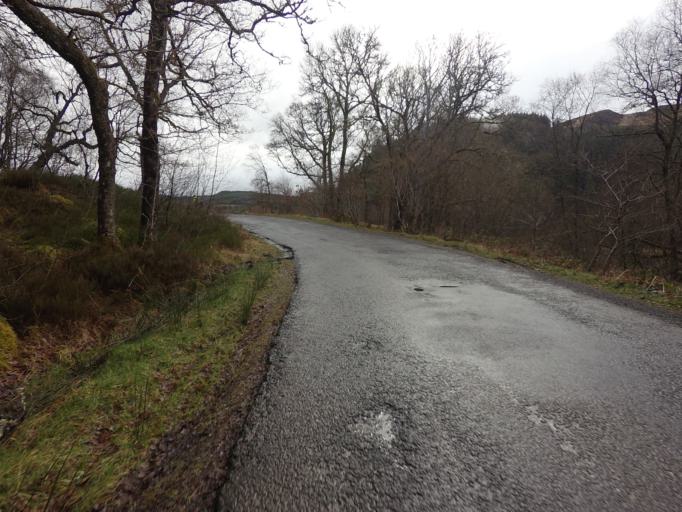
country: GB
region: Scotland
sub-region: West Dunbartonshire
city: Balloch
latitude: 56.2064
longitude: -4.5341
